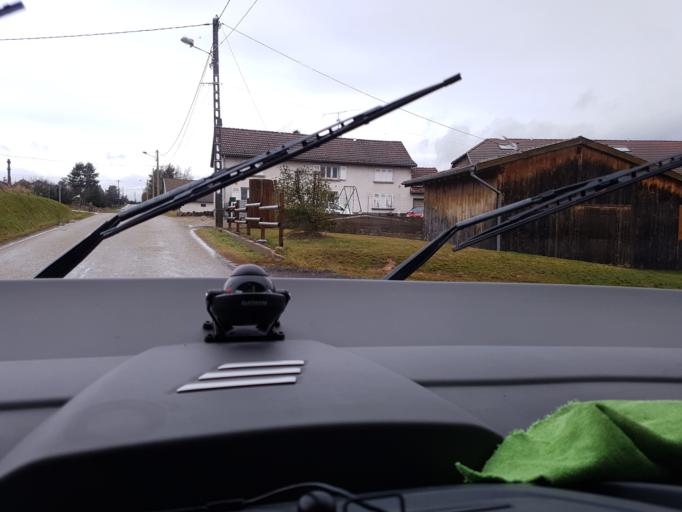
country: FR
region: Lorraine
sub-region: Departement des Vosges
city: Saint-Michel-sur-Meurthe
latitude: 48.3066
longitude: 6.9074
